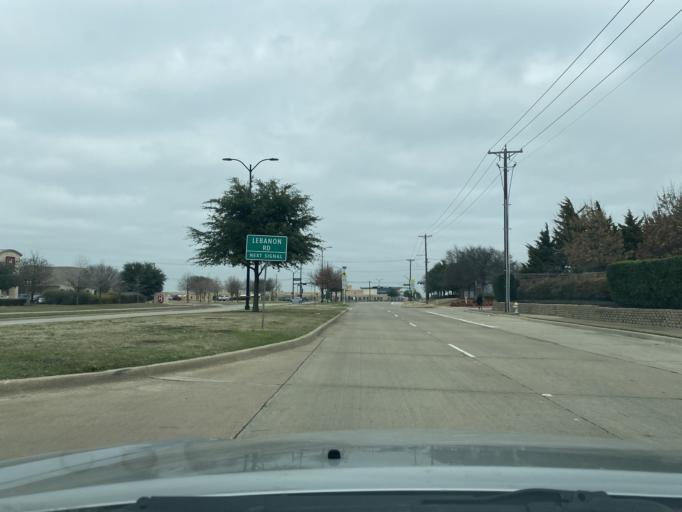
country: US
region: Texas
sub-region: Collin County
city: Frisco
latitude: 33.1173
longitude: -96.8016
